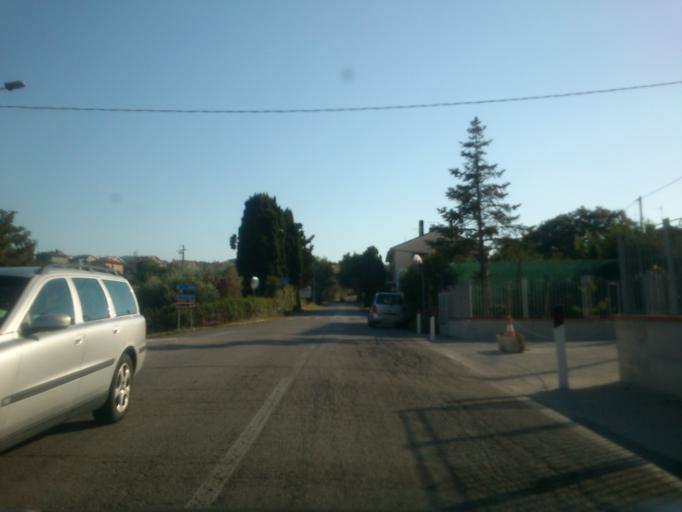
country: IT
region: The Marches
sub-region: Provincia di Pesaro e Urbino
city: Mombaroccio
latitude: 43.8113
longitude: 12.8603
